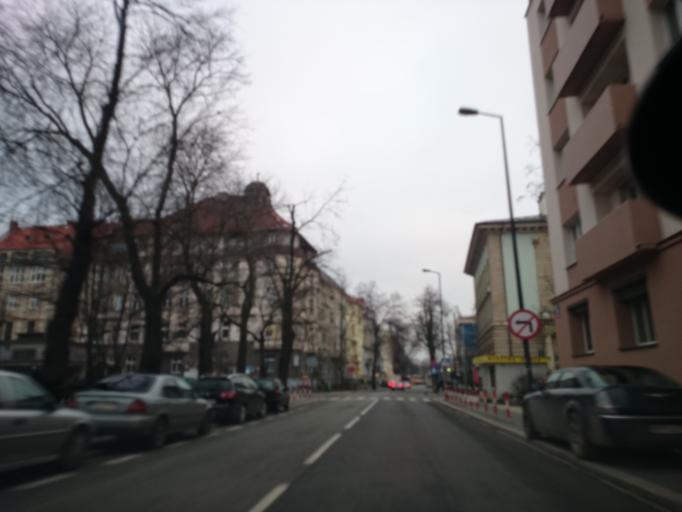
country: PL
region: Opole Voivodeship
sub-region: Powiat opolski
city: Opole
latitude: 50.6652
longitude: 17.9272
